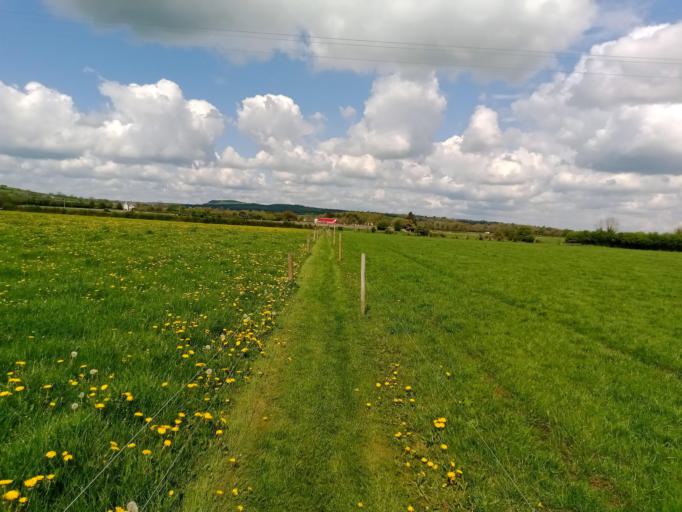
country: IE
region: Leinster
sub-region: Kilkenny
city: Ballyragget
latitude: 52.7329
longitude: -7.4165
